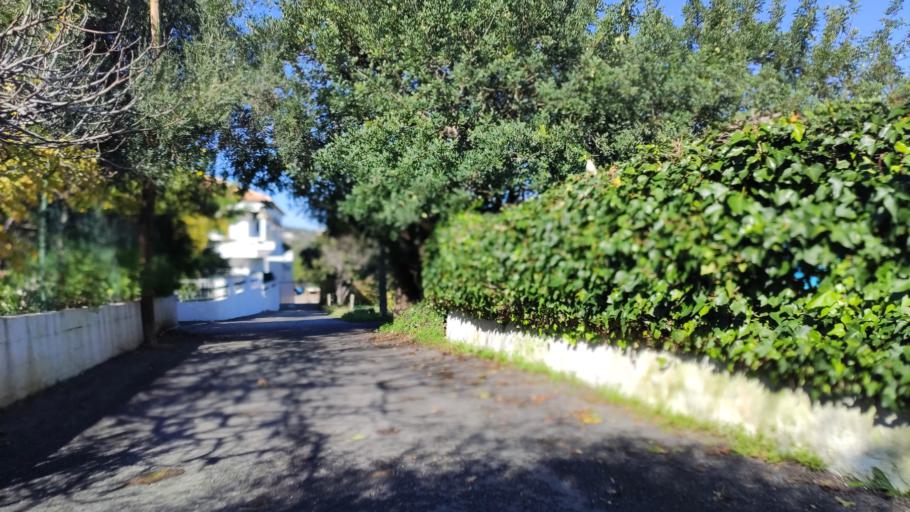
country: PT
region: Faro
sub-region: Sao Bras de Alportel
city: Sao Bras de Alportel
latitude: 37.1532
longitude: -7.8744
